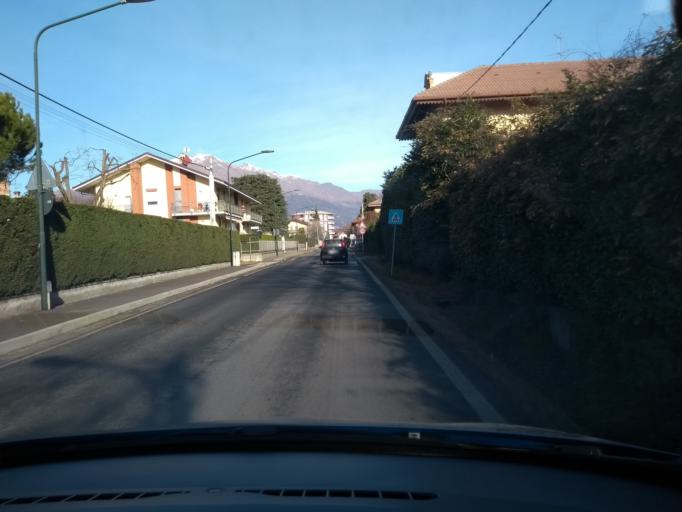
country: IT
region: Piedmont
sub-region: Provincia di Torino
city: Valperga
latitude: 45.3667
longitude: 7.6597
